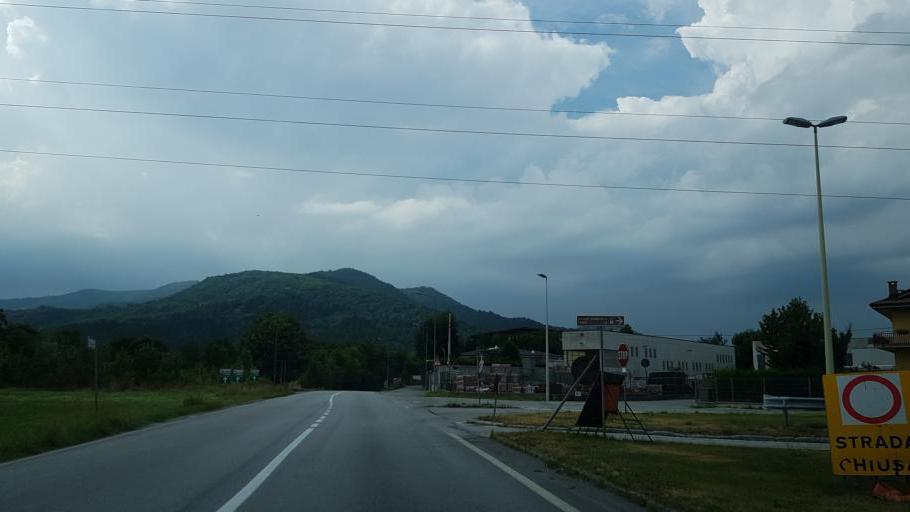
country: IT
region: Piedmont
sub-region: Provincia di Cuneo
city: Borgo San Dalmazzo
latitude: 44.3385
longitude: 7.4779
